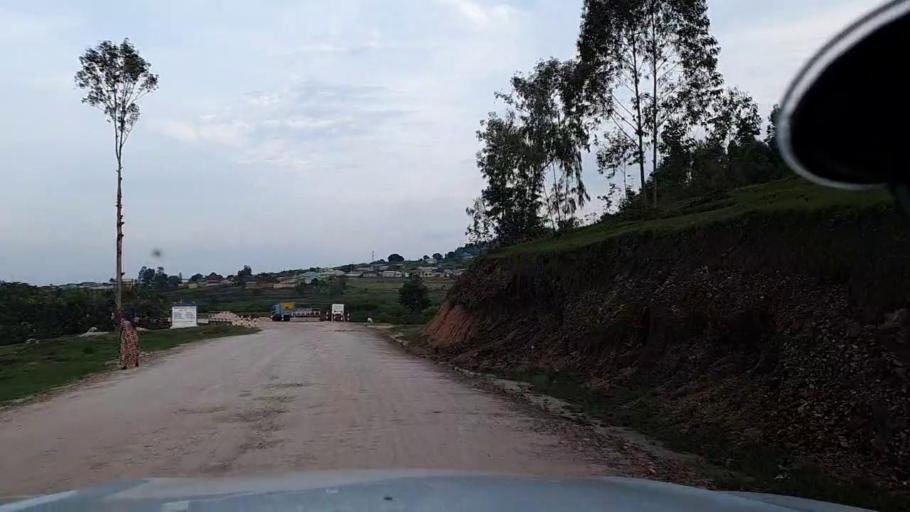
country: RW
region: Southern Province
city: Nyanza
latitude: -2.2264
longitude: 29.6551
